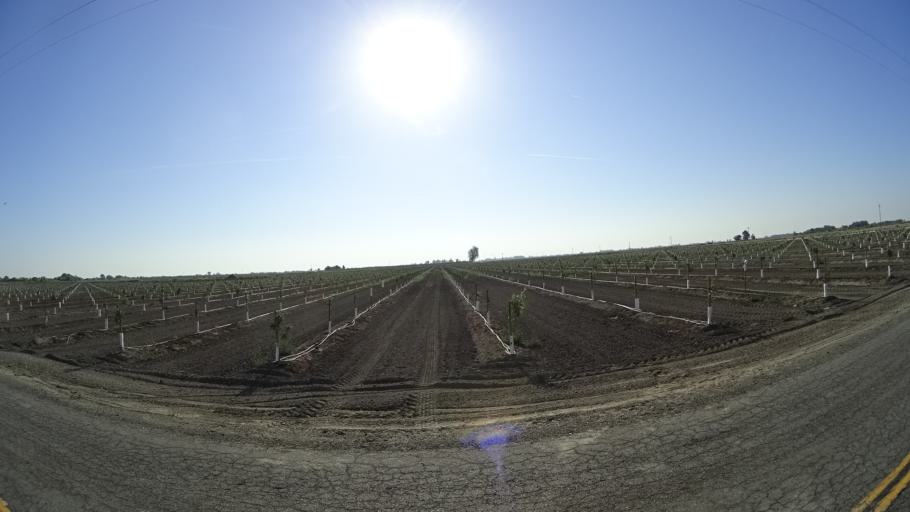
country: US
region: California
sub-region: Fresno County
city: Riverdale
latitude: 36.3808
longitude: -119.9278
